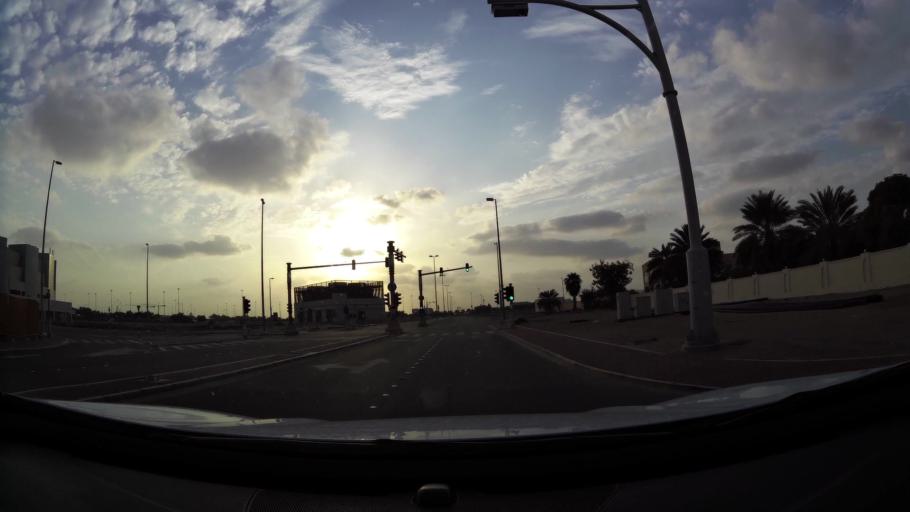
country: AE
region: Abu Dhabi
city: Abu Dhabi
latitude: 24.3786
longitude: 54.5308
